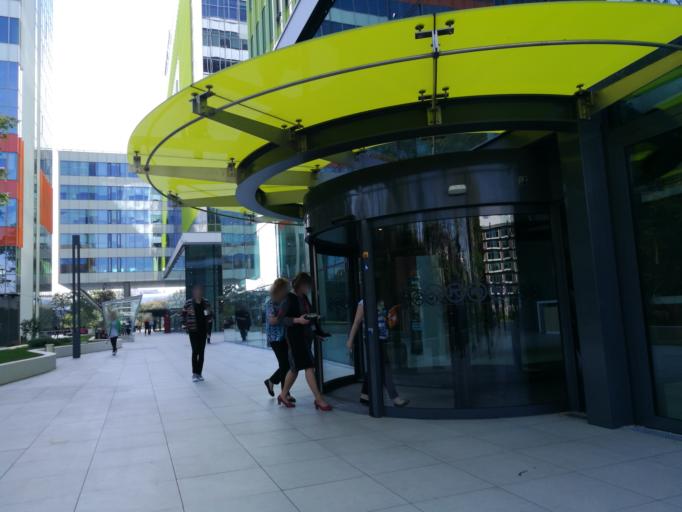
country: RO
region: Bucuresti
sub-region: Municipiul Bucuresti
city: Bucharest
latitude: 44.4798
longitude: 26.1064
